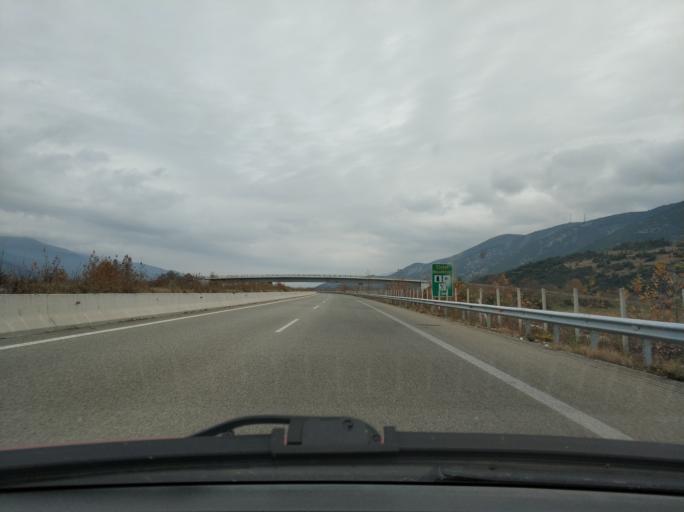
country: GR
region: East Macedonia and Thrace
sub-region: Nomos Kavalas
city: Nikisiani
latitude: 40.8278
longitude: 24.0954
